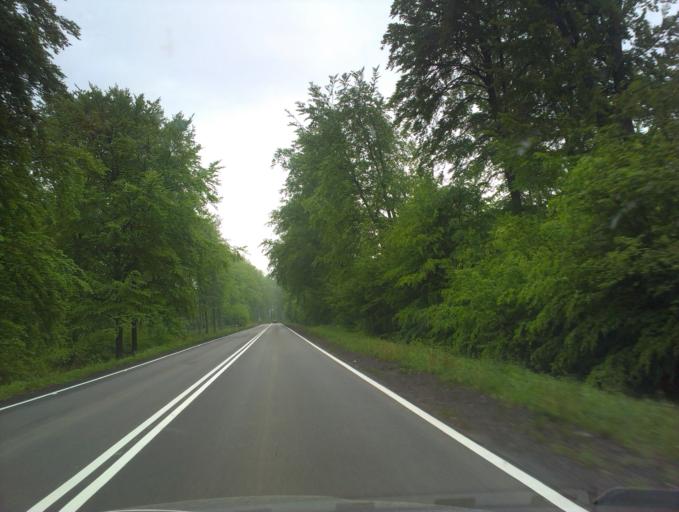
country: PL
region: West Pomeranian Voivodeship
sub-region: Powiat koszalinski
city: Bobolice
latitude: 53.9204
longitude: 16.6039
